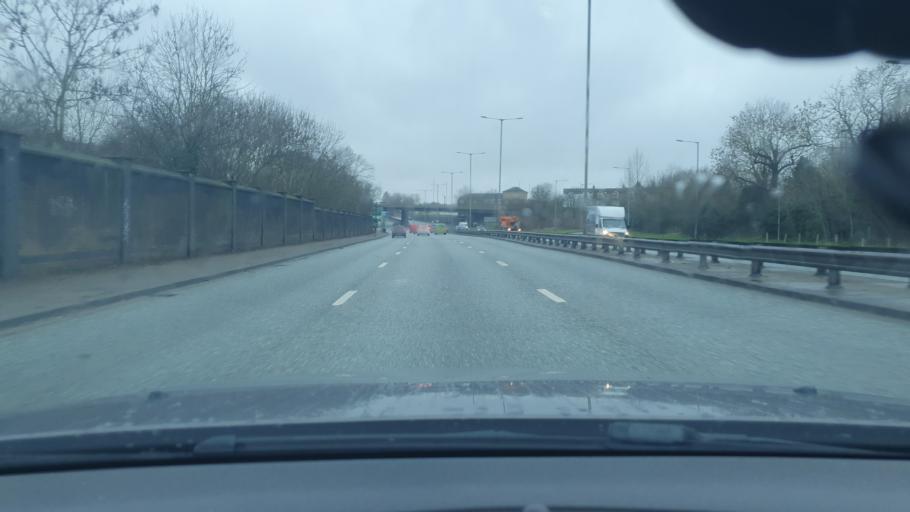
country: GB
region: England
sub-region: Greater London
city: Hendon
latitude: 51.6029
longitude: -0.1698
